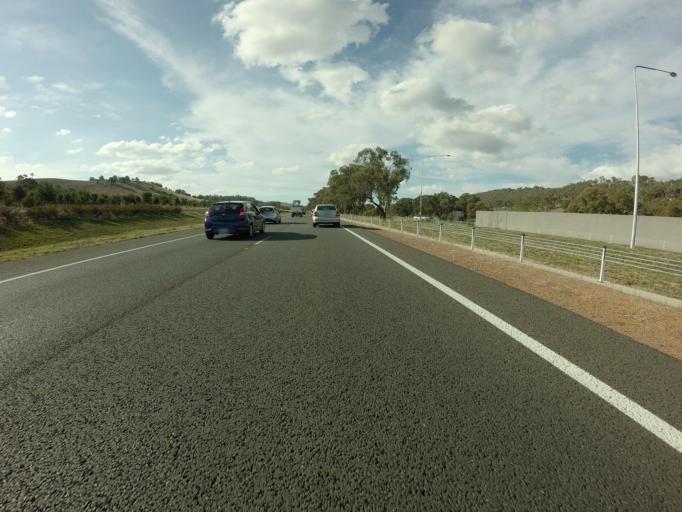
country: AU
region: Australian Capital Territory
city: Canberra
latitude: -35.2277
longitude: 149.1961
